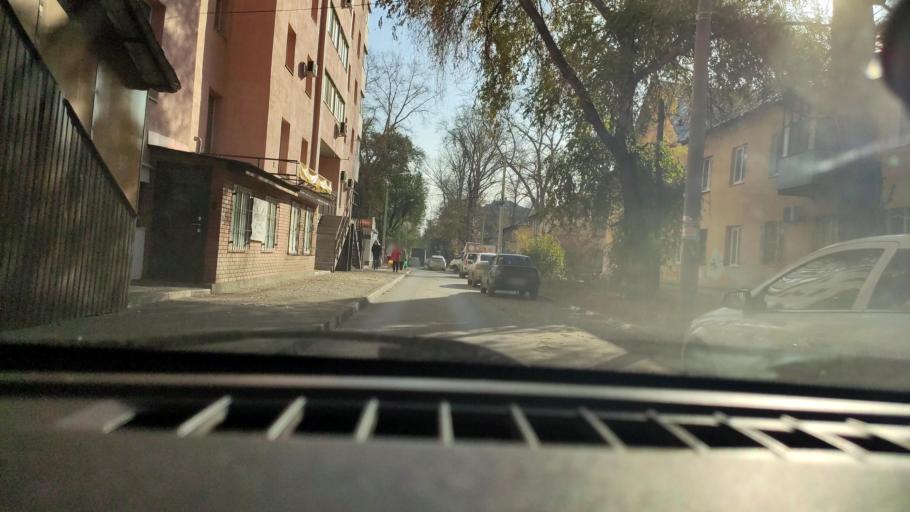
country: RU
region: Samara
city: Samara
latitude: 53.2288
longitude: 50.2610
